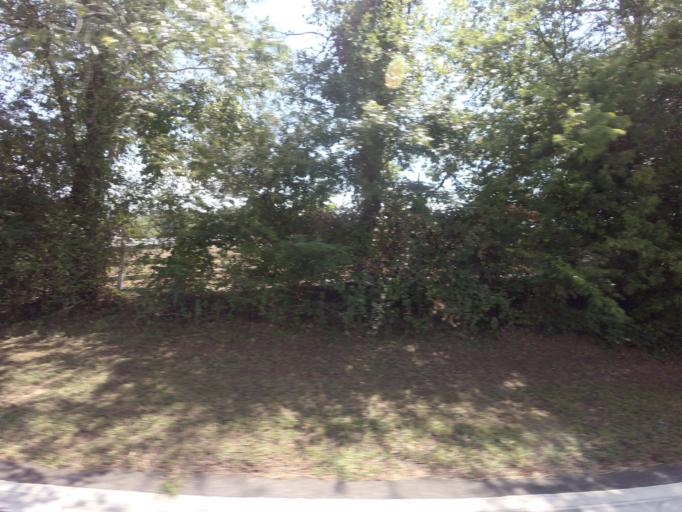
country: US
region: Georgia
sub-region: Fulton County
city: Johns Creek
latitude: 34.0417
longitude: -84.2038
